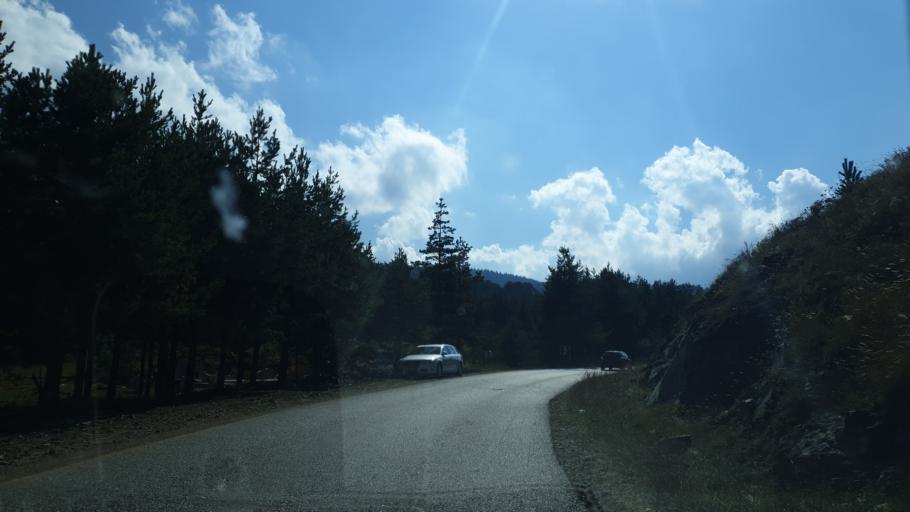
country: RS
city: Zlatibor
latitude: 43.6743
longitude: 19.6540
